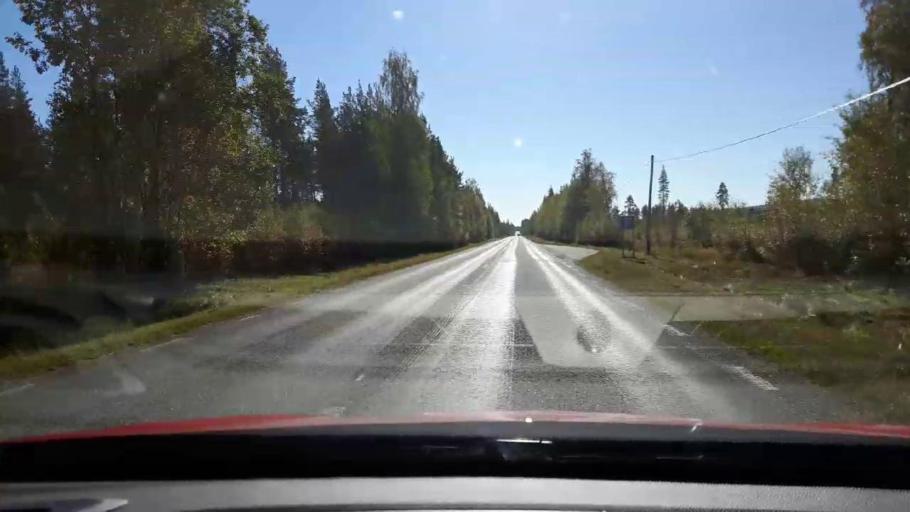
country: SE
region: Jaemtland
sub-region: Harjedalens Kommun
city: Sveg
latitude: 62.4058
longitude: 13.9266
